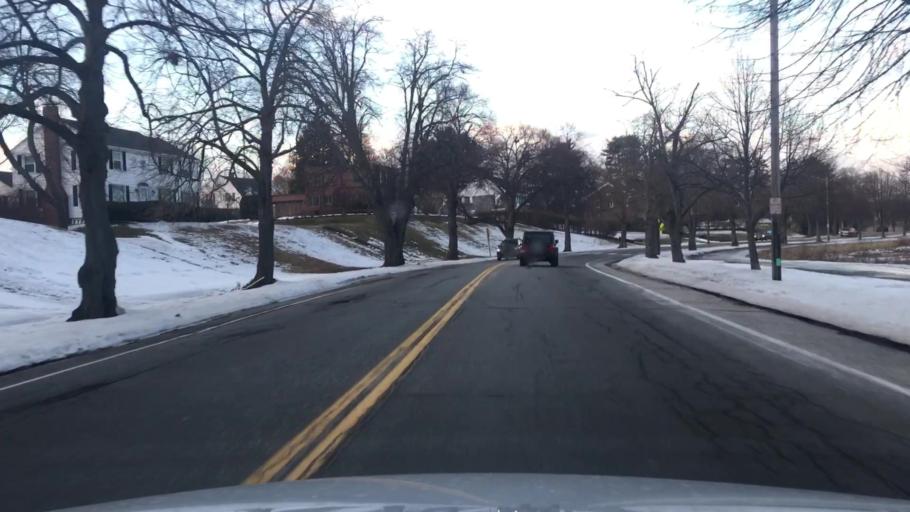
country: US
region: Maine
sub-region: Cumberland County
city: Portland
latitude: 43.6725
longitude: -70.2774
